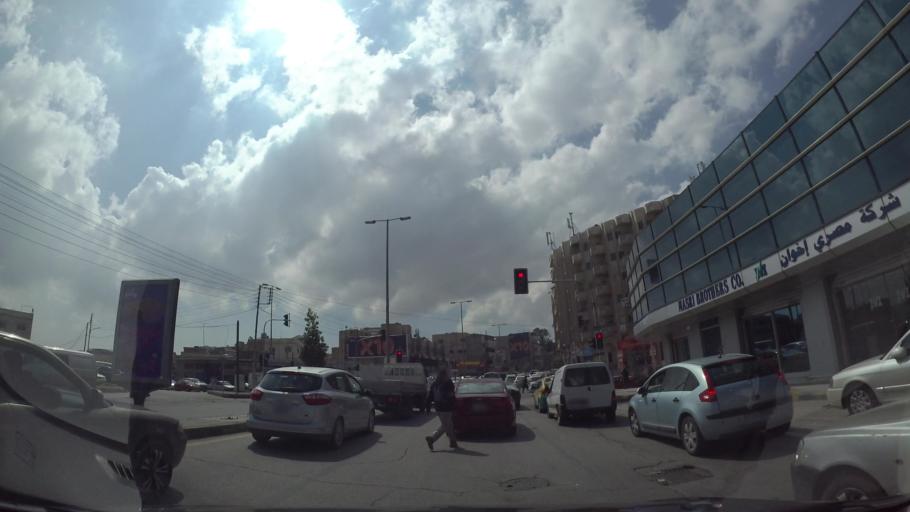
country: JO
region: Amman
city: Amman
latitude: 31.9828
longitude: 35.9933
